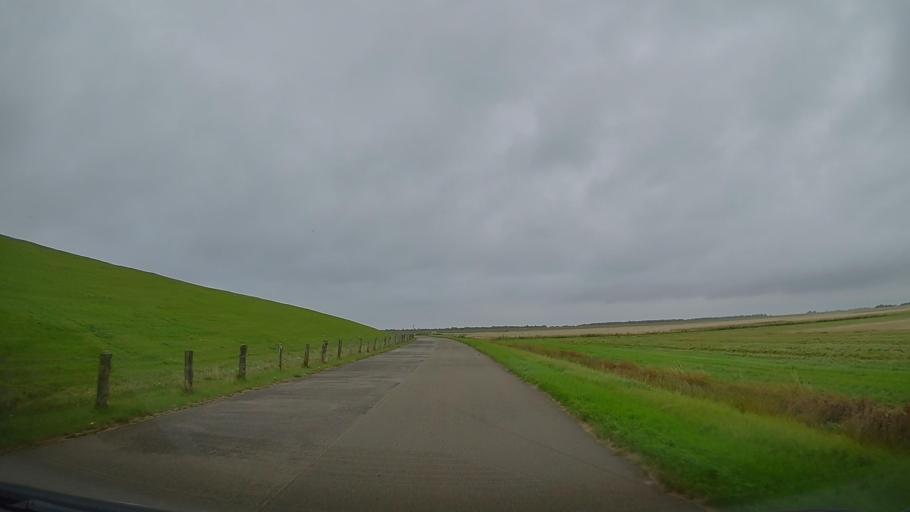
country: DE
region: Schleswig-Holstein
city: Busenwurth
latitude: 54.0612
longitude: 8.9869
